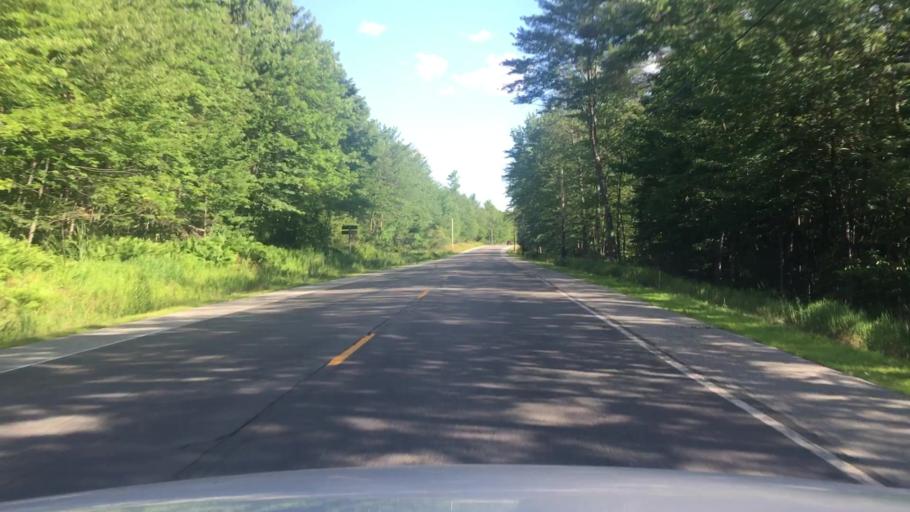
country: US
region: Maine
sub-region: Franklin County
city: Jay
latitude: 44.5414
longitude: -70.2356
